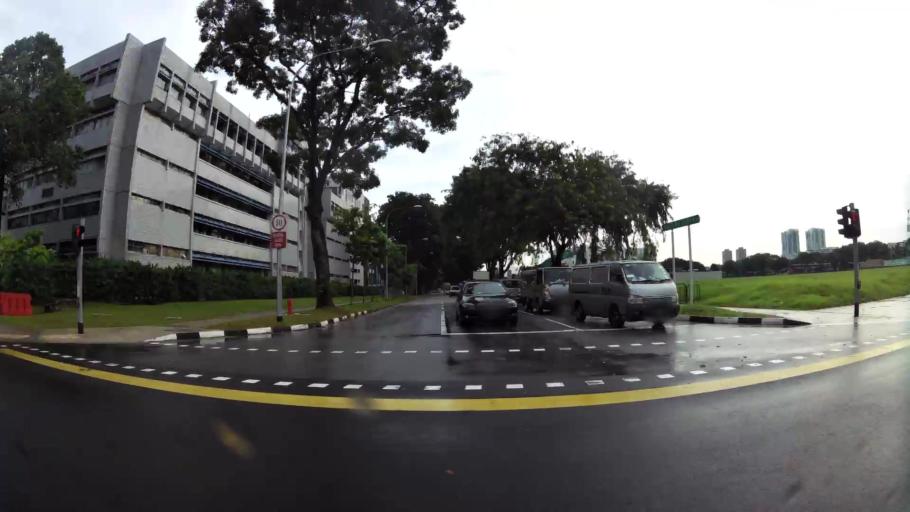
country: SG
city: Singapore
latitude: 1.3778
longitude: 103.8634
